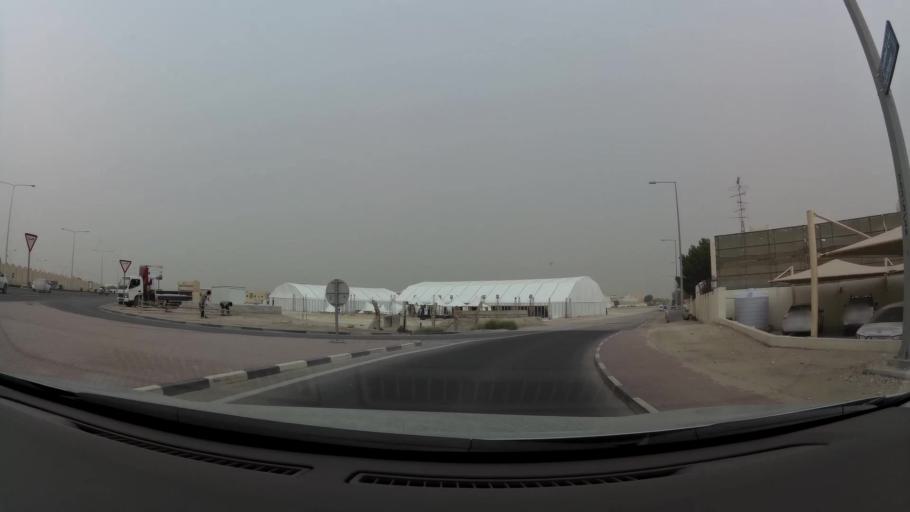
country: QA
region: Baladiyat ad Dawhah
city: Doha
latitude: 25.2537
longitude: 51.4911
